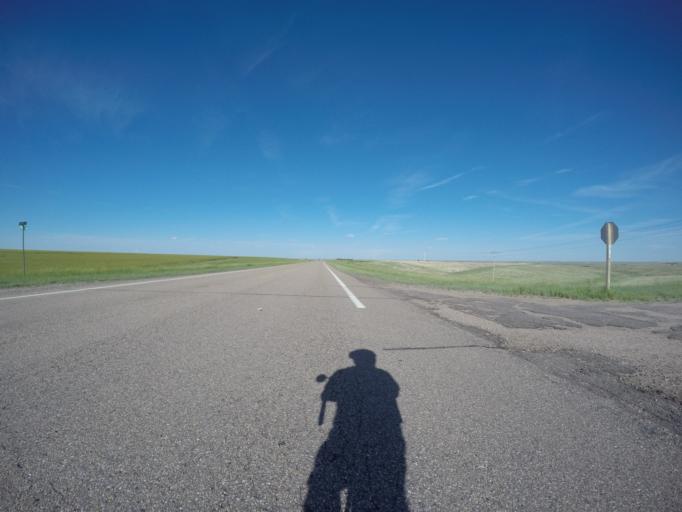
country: US
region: Kansas
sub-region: Cheyenne County
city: Saint Francis
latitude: 39.7569
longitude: -101.9186
